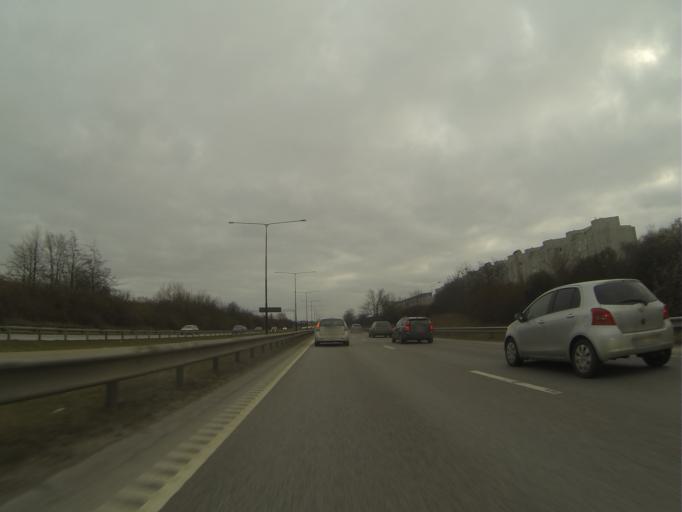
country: SE
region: Skane
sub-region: Burlovs Kommun
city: Arloev
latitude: 55.5919
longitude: 13.0541
